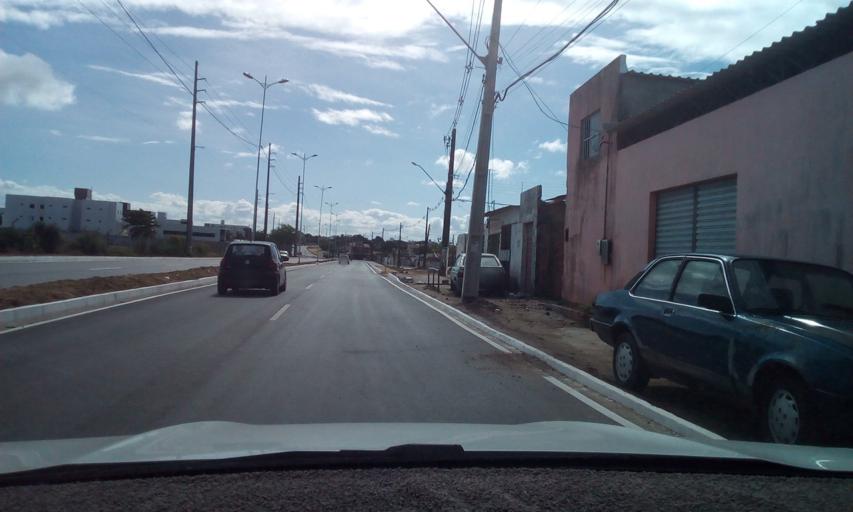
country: BR
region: Paraiba
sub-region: Conde
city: Conde
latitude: -7.2077
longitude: -34.8470
